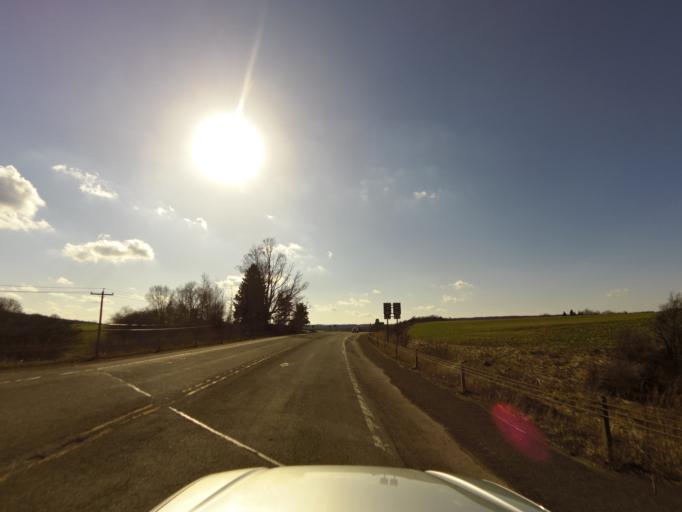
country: US
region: New York
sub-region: Wyoming County
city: Arcade
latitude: 42.4365
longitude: -78.3268
